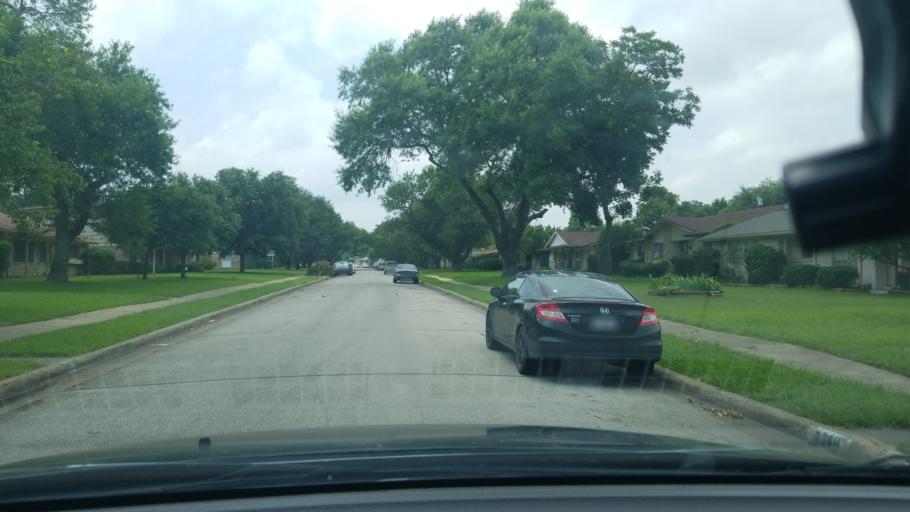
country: US
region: Texas
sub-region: Dallas County
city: Mesquite
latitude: 32.7975
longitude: -96.6464
